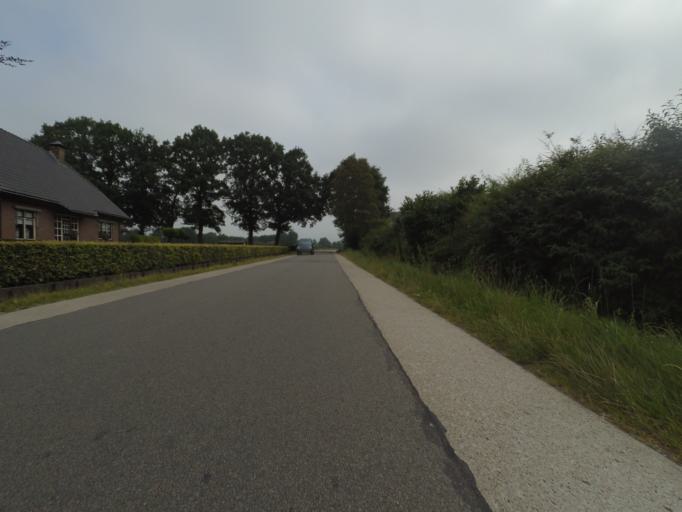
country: NL
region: Gelderland
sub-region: Gemeente Barneveld
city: Kootwijkerbroek
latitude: 52.1429
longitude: 5.6574
